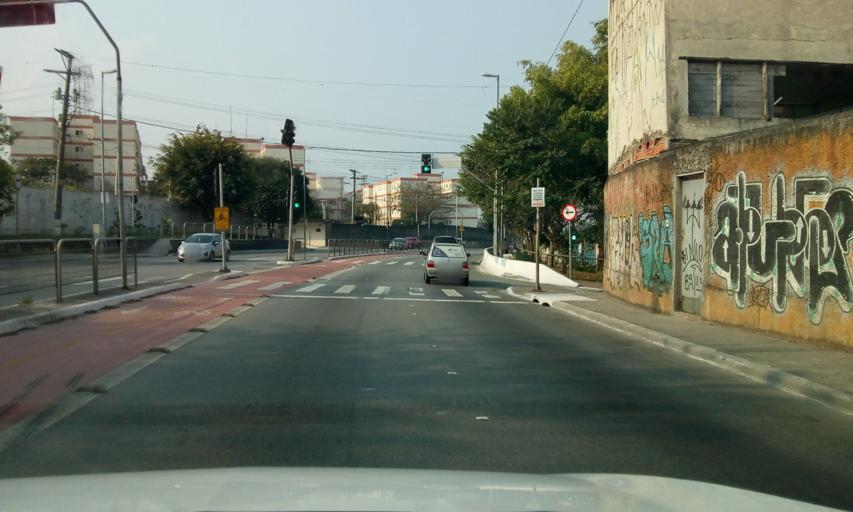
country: BR
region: Sao Paulo
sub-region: Diadema
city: Diadema
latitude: -23.7047
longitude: -46.6872
